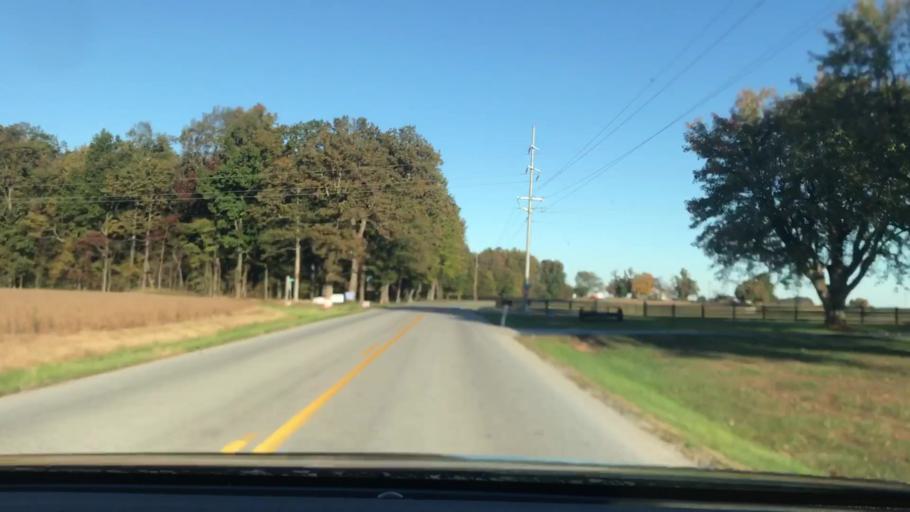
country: US
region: Kentucky
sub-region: Simpson County
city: Franklin
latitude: 36.7829
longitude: -86.6244
